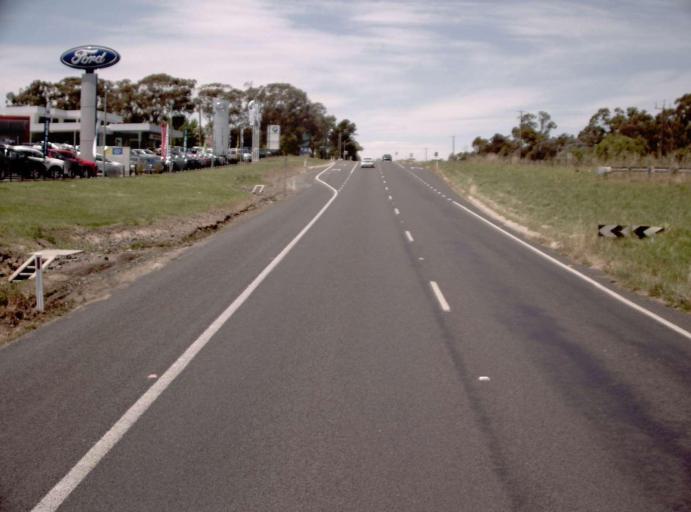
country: AU
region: Victoria
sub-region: Latrobe
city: Traralgon
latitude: -38.2076
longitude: 146.5005
